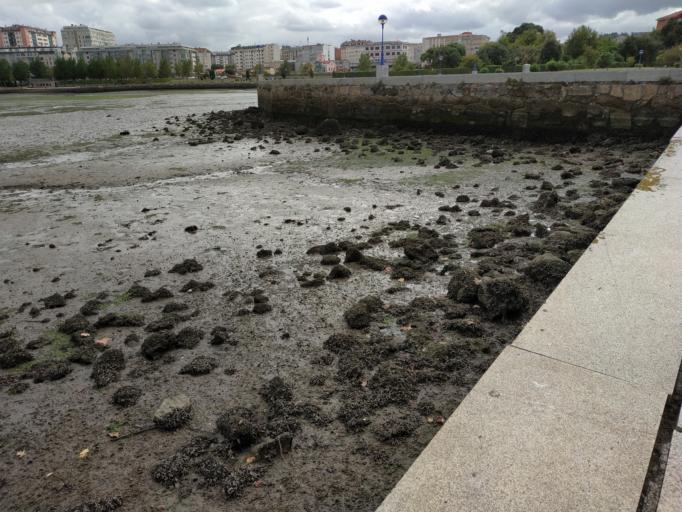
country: ES
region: Galicia
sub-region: Provincia da Coruna
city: Cambre
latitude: 43.3215
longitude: -8.3704
